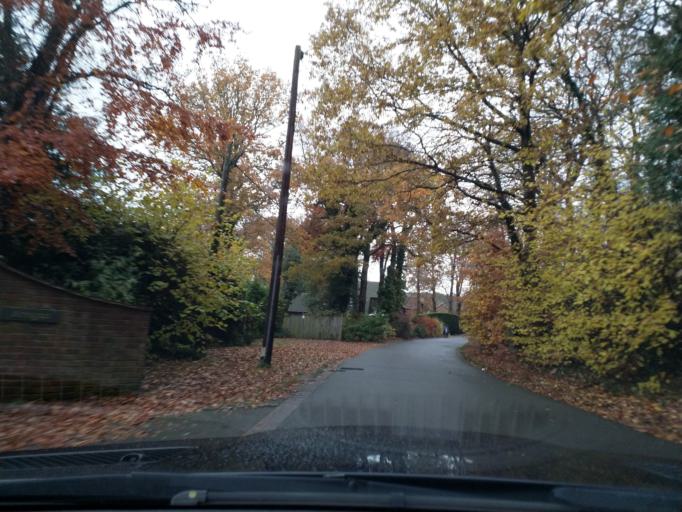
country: GB
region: England
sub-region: Surrey
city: Frimley
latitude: 51.3080
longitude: -0.7202
